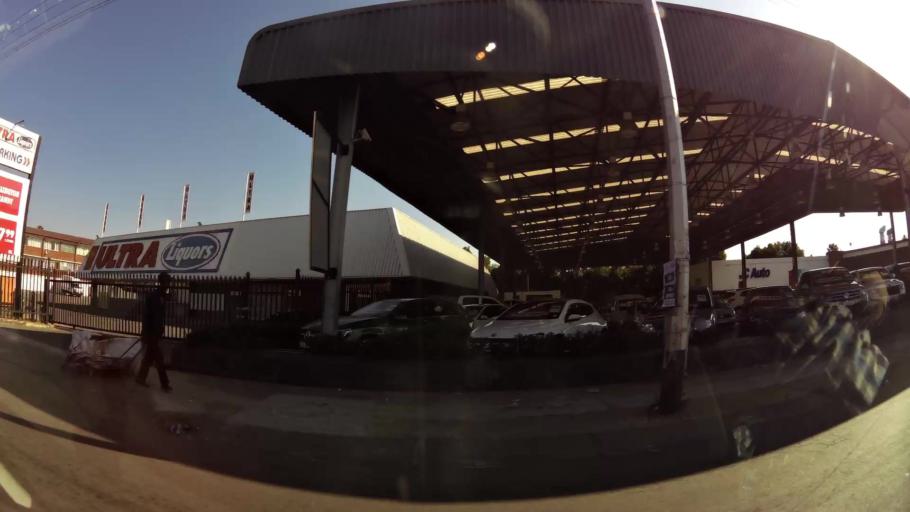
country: ZA
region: Gauteng
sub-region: City of Tshwane Metropolitan Municipality
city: Pretoria
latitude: -25.7096
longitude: 28.2010
